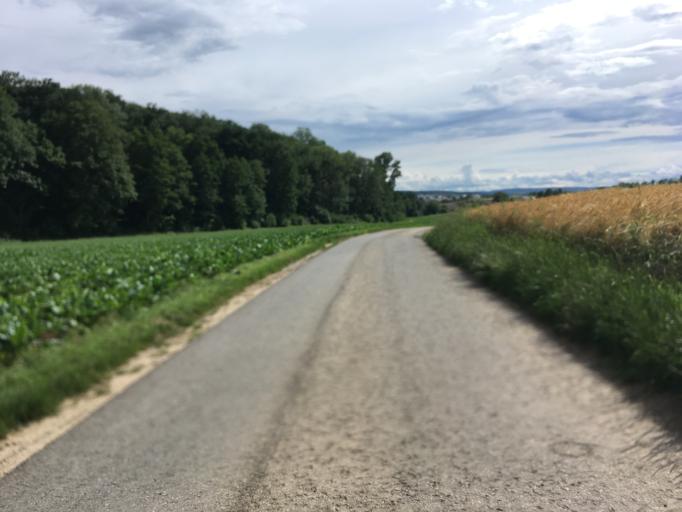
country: DE
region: Baden-Wuerttemberg
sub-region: Regierungsbezirk Stuttgart
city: Oberriexingen
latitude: 48.9411
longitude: 9.0304
